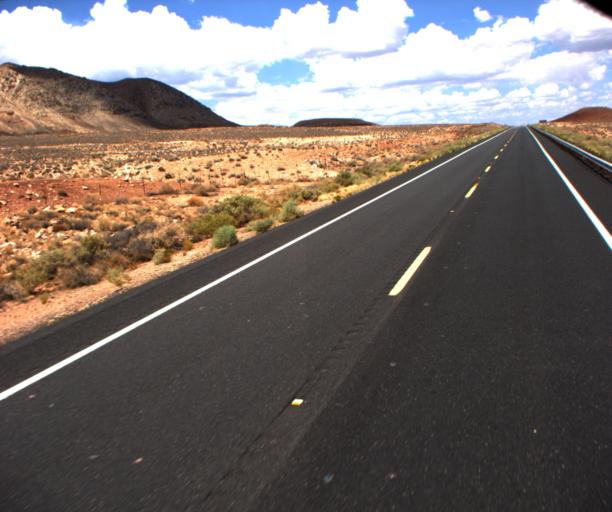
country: US
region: Arizona
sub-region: Coconino County
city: Tuba City
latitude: 35.8991
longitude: -111.5421
